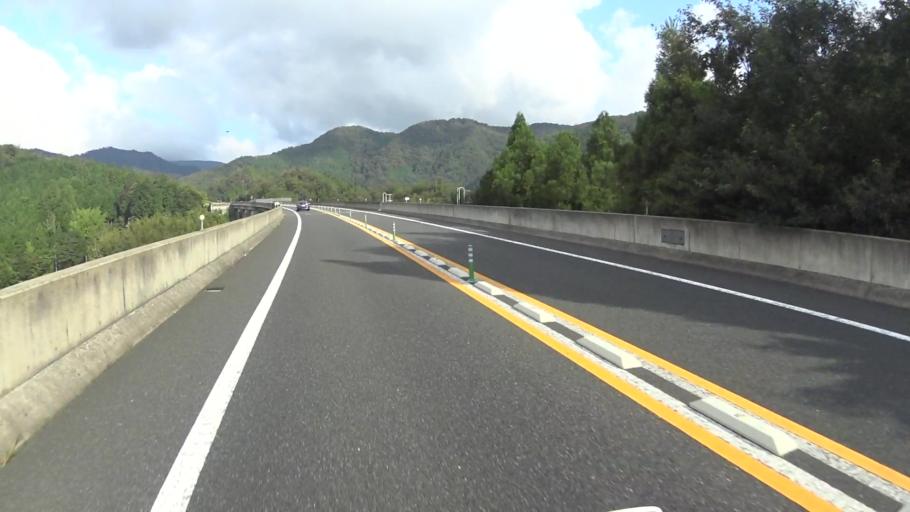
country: JP
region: Kyoto
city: Miyazu
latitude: 35.4470
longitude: 135.1857
